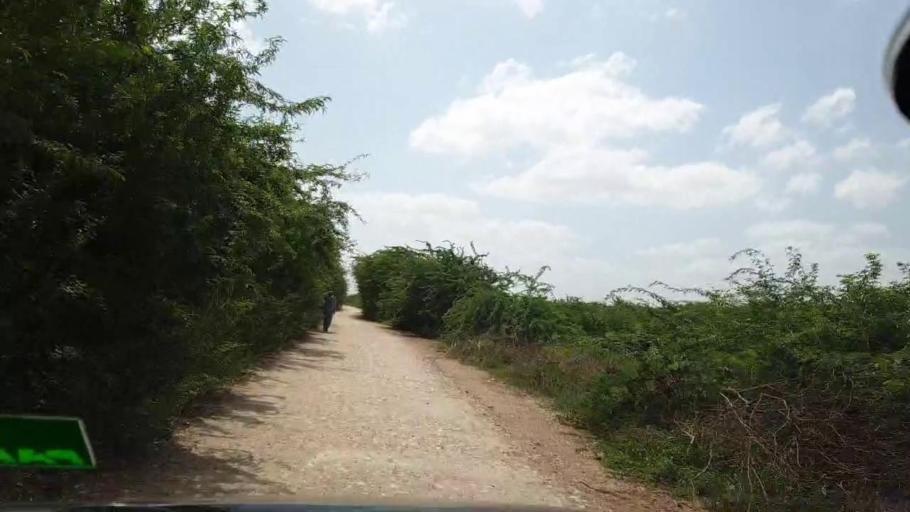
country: PK
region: Sindh
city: Kadhan
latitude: 24.5565
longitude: 69.2113
